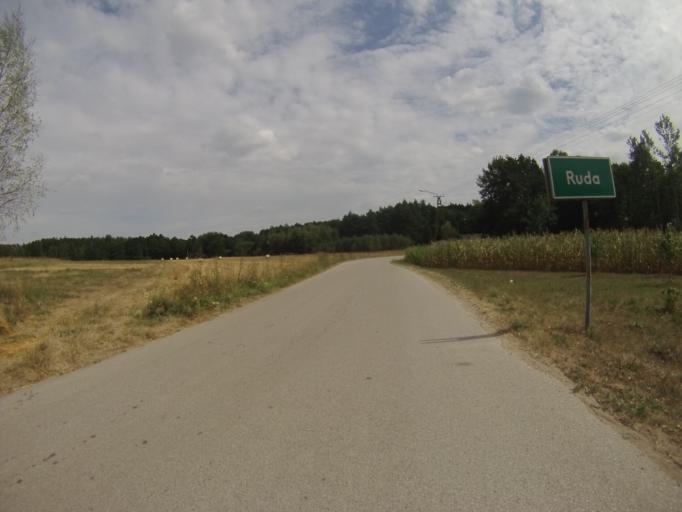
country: PL
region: Swietokrzyskie
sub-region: Powiat kielecki
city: Lagow
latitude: 50.7496
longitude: 21.1287
